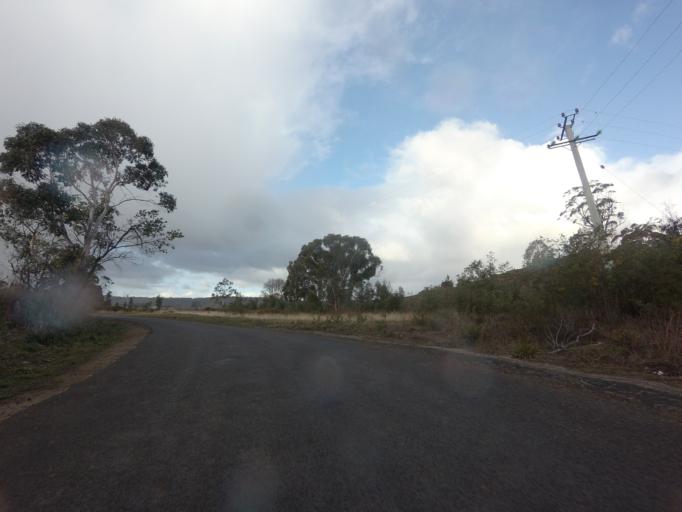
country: AU
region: Tasmania
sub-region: Break O'Day
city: St Helens
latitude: -42.0071
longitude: 148.0764
